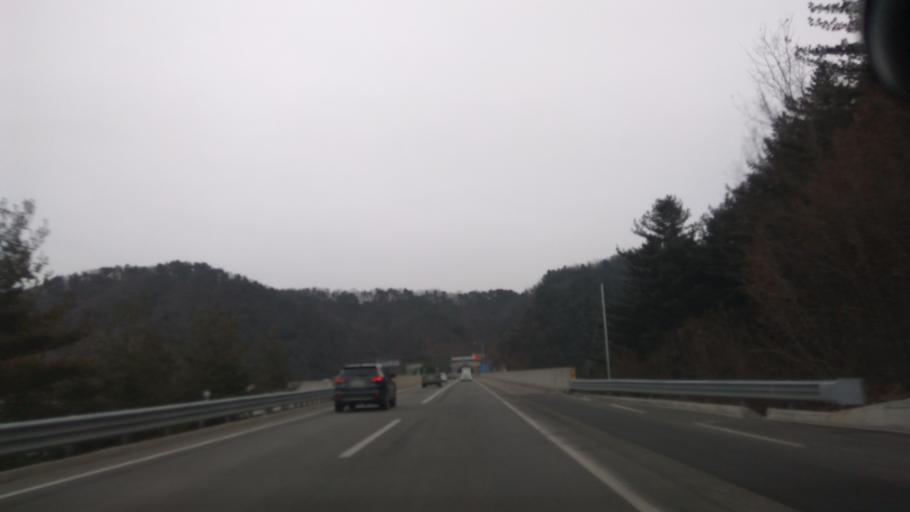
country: KR
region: Gangwon-do
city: Sindong
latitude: 37.7403
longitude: 127.6536
